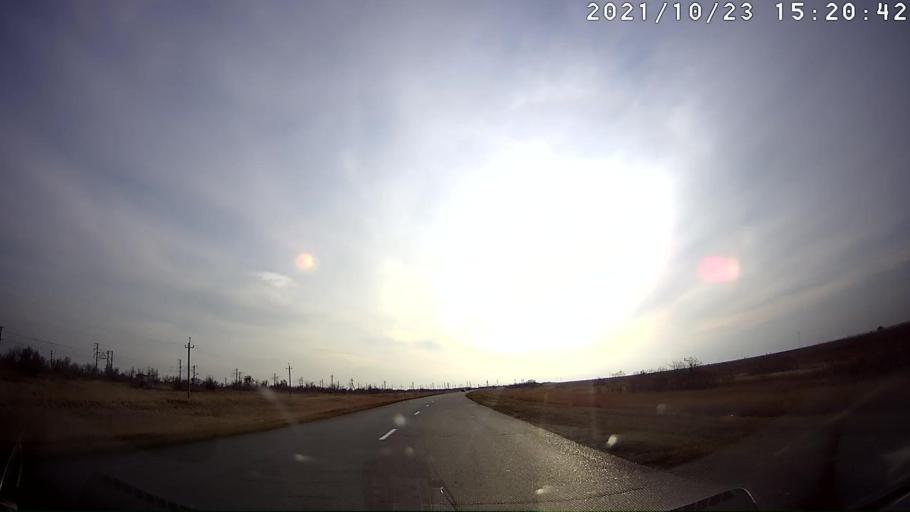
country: RU
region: Volgograd
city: Bereslavka
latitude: 48.3186
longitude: 44.3231
